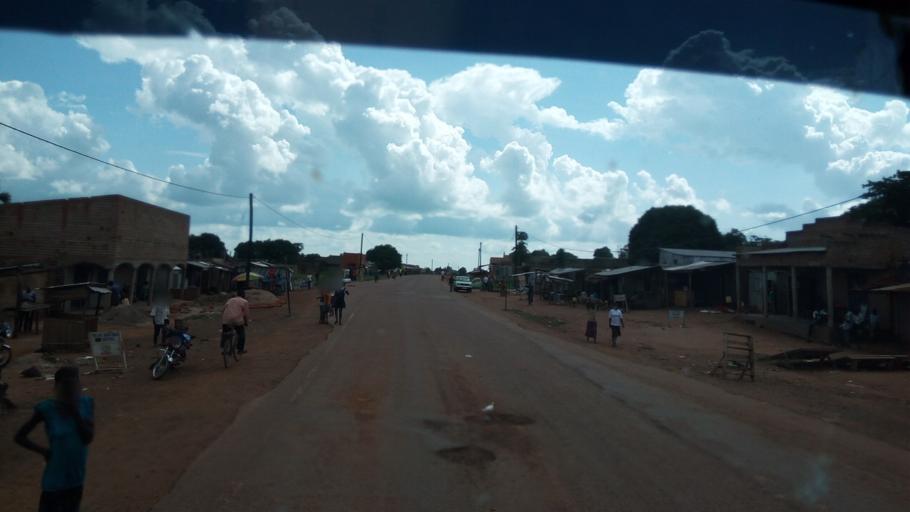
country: UG
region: Northern Region
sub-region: Nwoya District
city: Nwoya
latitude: 2.5361
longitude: 31.8846
